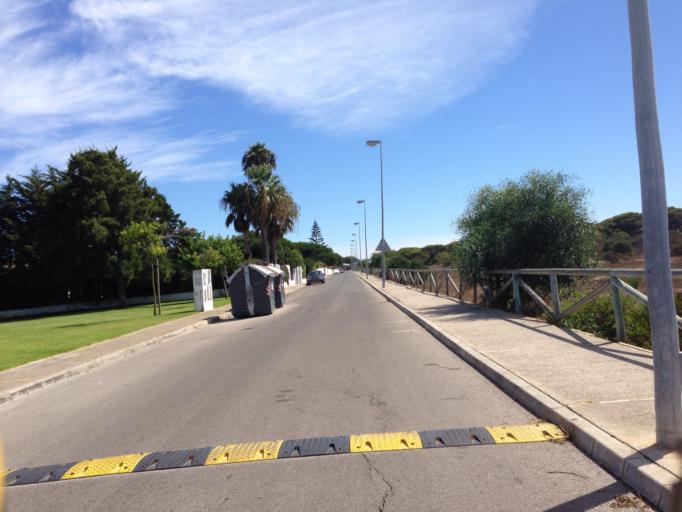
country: ES
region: Andalusia
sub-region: Provincia de Cadiz
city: Chiclana de la Frontera
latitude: 36.3854
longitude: -6.2035
